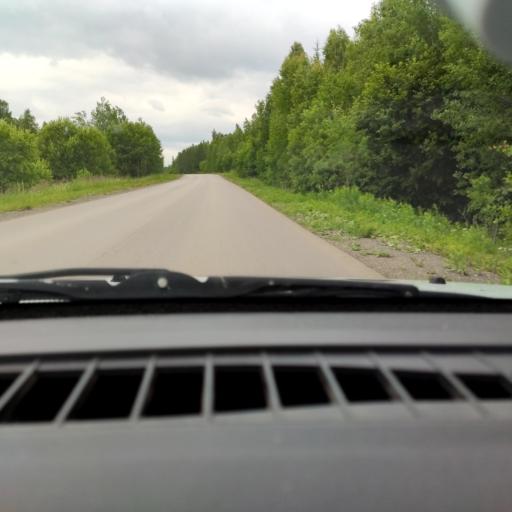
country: RU
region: Perm
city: Orda
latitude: 57.1268
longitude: 56.6875
